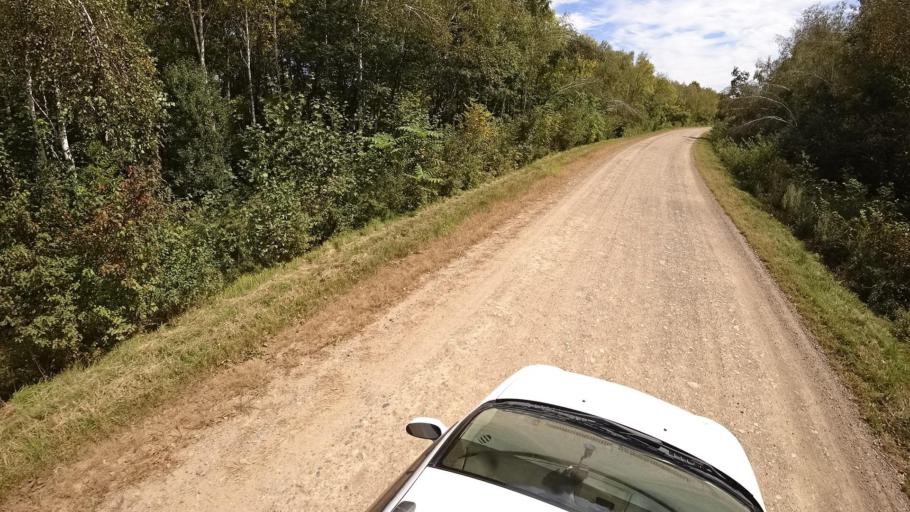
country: RU
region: Primorskiy
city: Yakovlevka
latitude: 44.6632
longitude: 133.7234
